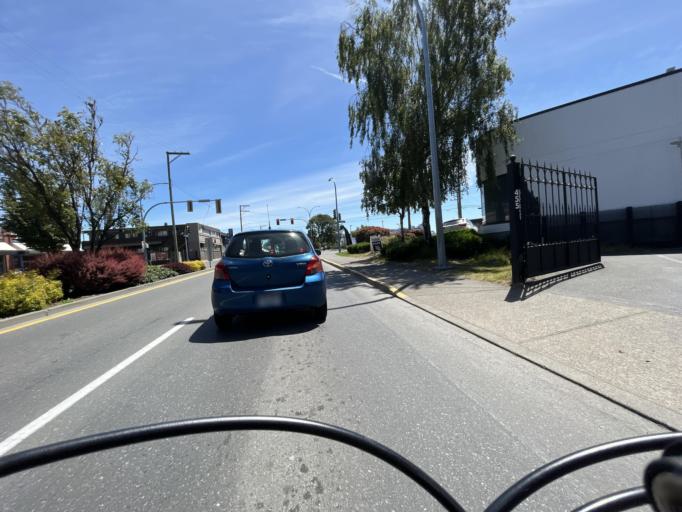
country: CA
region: British Columbia
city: Victoria
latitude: 48.4408
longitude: -123.3740
